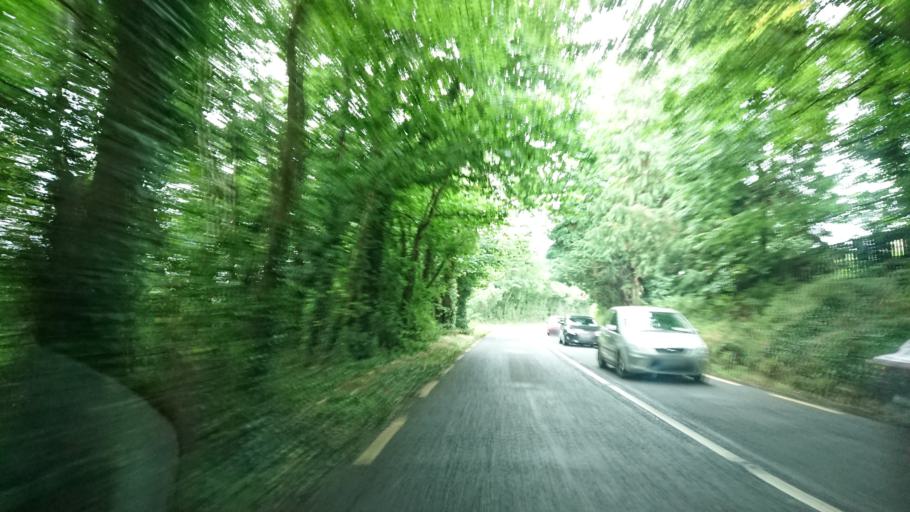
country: IE
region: Munster
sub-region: Ciarrai
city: Killorglin
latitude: 52.1011
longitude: -9.7151
